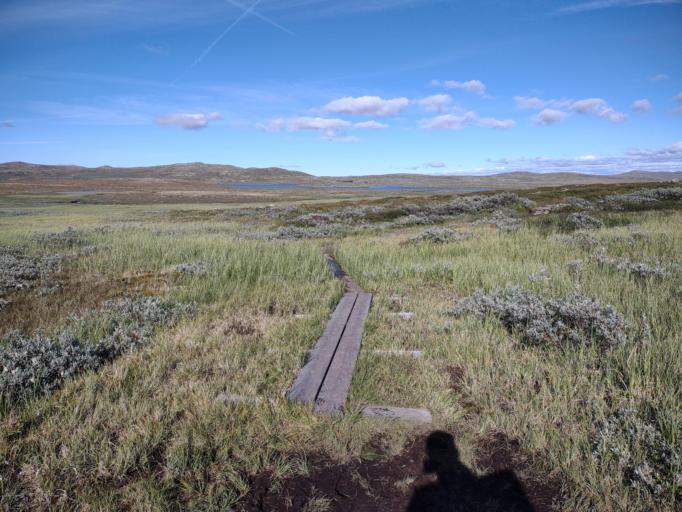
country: NO
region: Hordaland
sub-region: Eidfjord
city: Eidfjord
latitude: 60.1733
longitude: 7.4470
